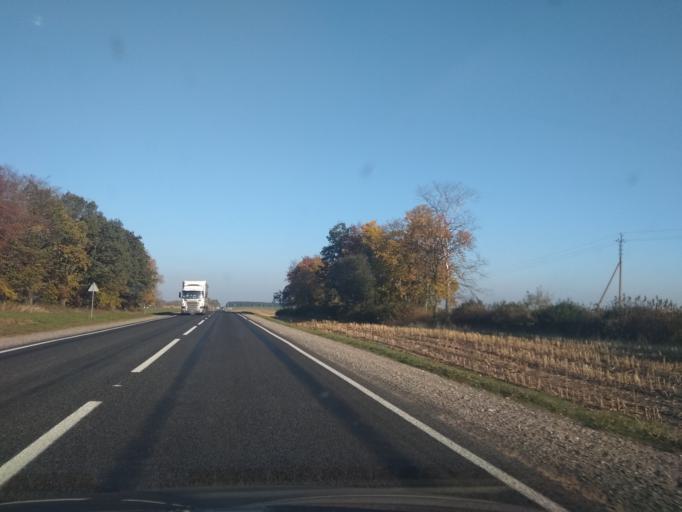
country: BY
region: Grodnenskaya
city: Svislach
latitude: 53.1341
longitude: 24.2309
